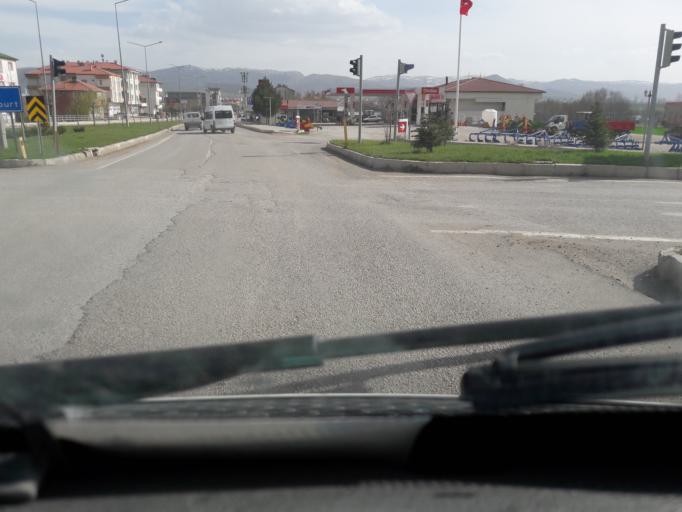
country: TR
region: Gumushane
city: Kelkit
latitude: 40.1428
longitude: 39.4332
